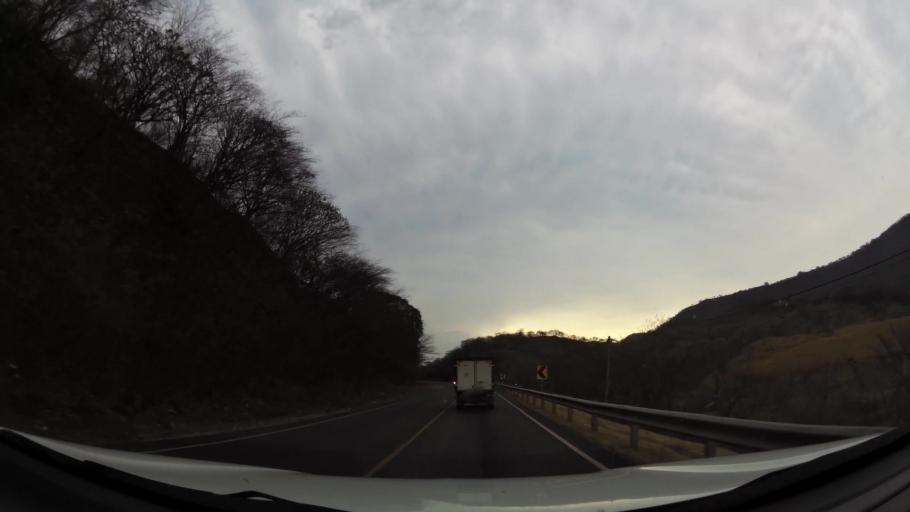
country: NI
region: Esteli
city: Esteli
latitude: 12.9423
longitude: -86.2178
